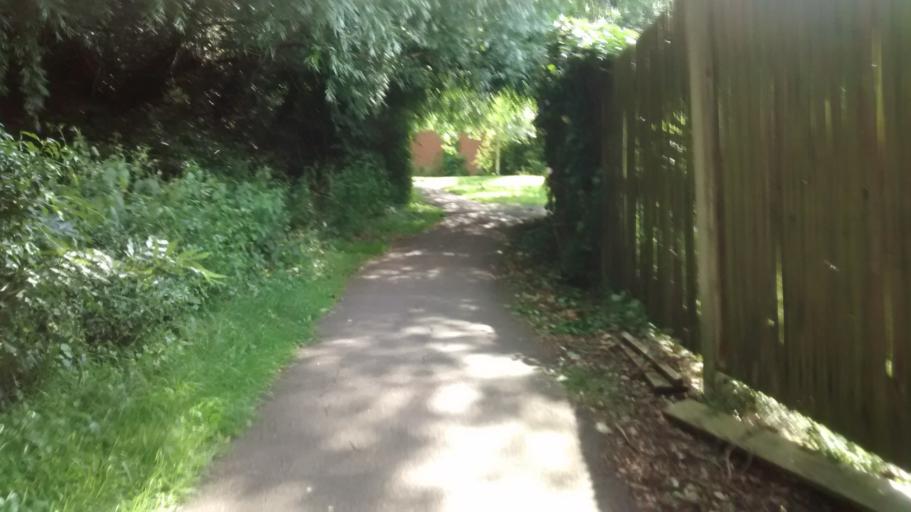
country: GB
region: England
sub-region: Cambridgeshire
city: Cambridge
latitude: 52.2020
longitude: 0.0978
